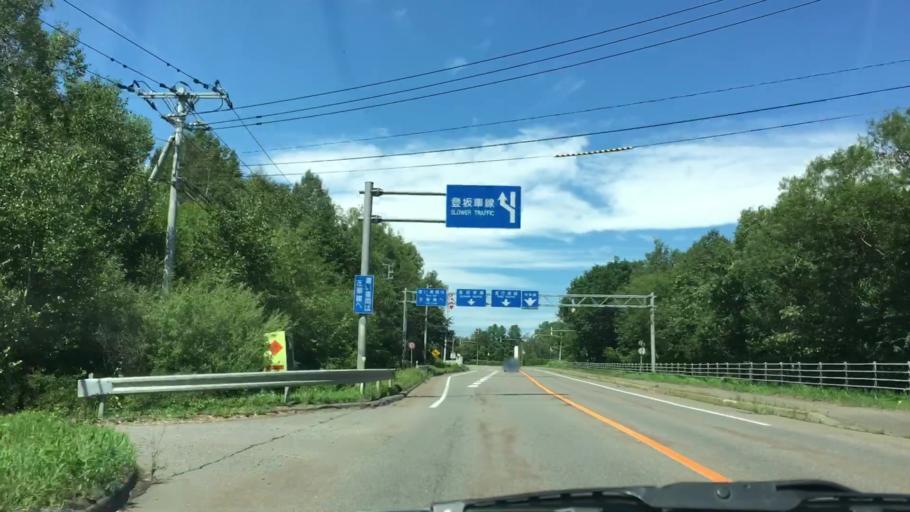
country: JP
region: Hokkaido
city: Otofuke
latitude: 43.2362
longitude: 143.5388
